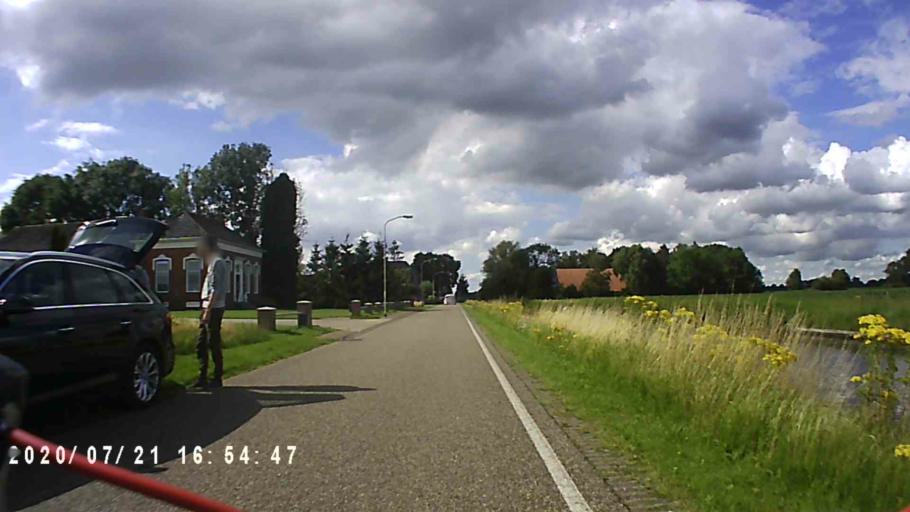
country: NL
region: Groningen
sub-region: Gemeente Hoogezand-Sappemeer
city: Hoogezand
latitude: 53.1293
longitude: 6.7668
